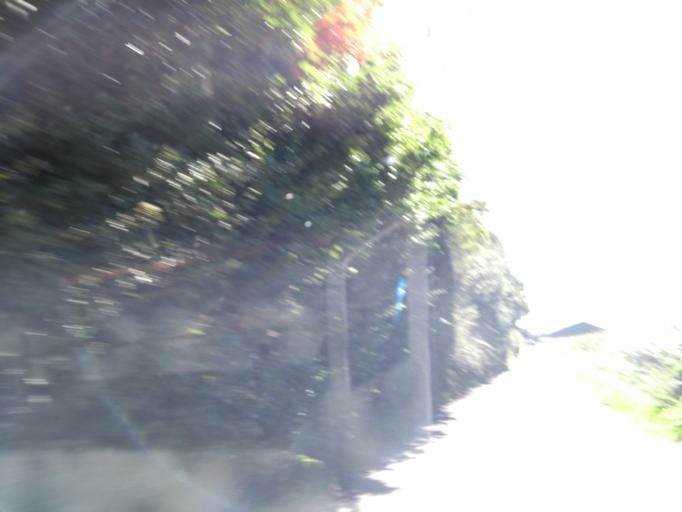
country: GB
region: England
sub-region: Somerset
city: Ilchester
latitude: 51.0536
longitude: -2.6825
